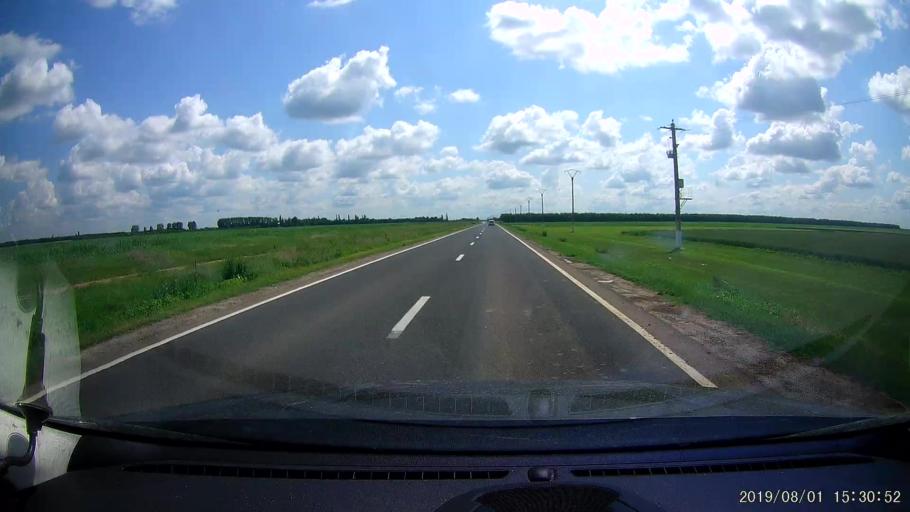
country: RO
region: Braila
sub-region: Comuna Viziru
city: Viziru
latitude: 44.9554
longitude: 27.6690
